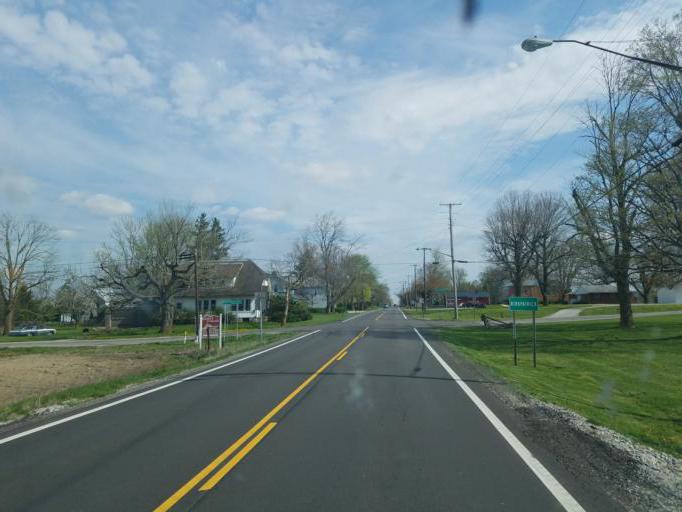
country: US
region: Ohio
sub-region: Crawford County
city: Bucyrus
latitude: 40.6882
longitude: -83.0087
